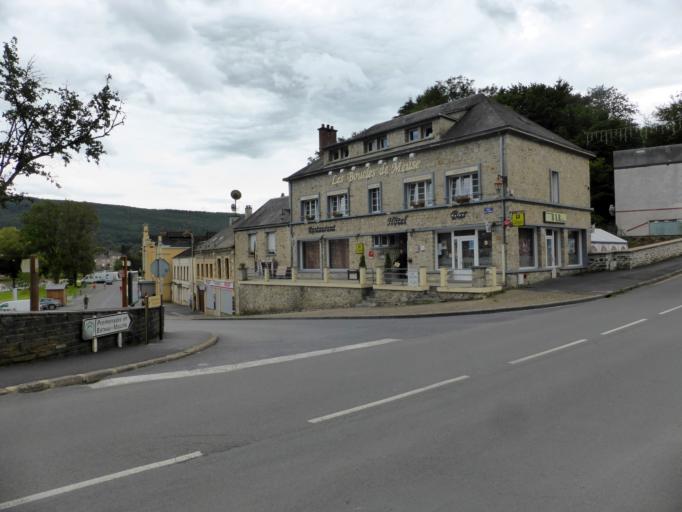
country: FR
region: Champagne-Ardenne
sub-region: Departement des Ardennes
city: Montherme
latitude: 49.8872
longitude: 4.7345
